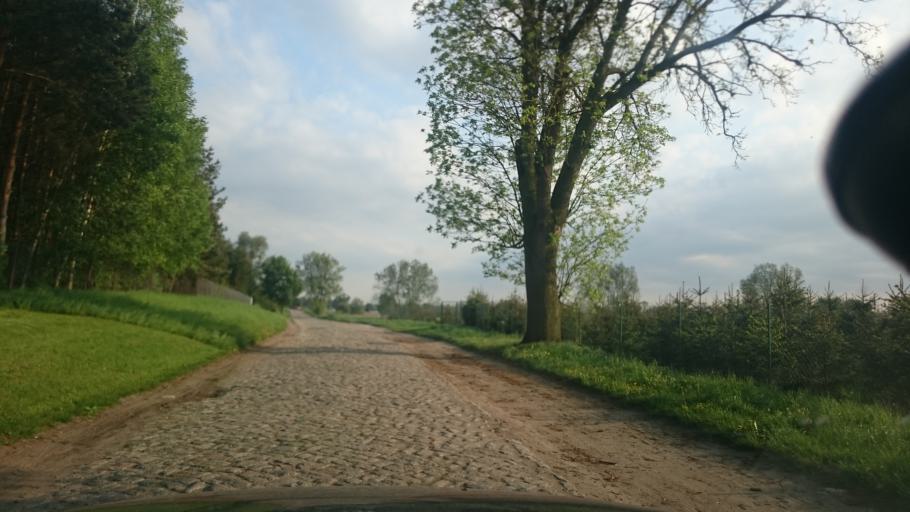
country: PL
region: Kujawsko-Pomorskie
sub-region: Grudziadz
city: Grudziadz
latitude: 53.4725
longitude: 18.8141
